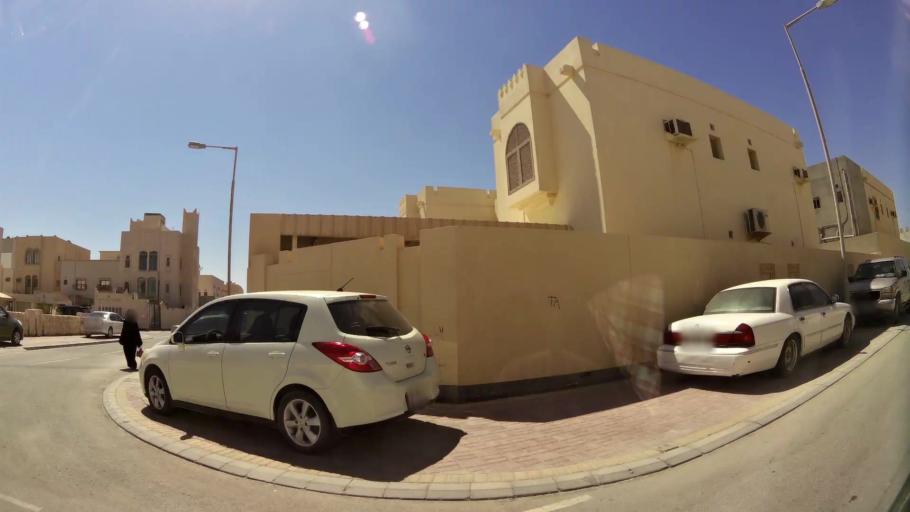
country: BH
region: Muharraq
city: Al Muharraq
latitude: 26.2680
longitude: 50.5981
